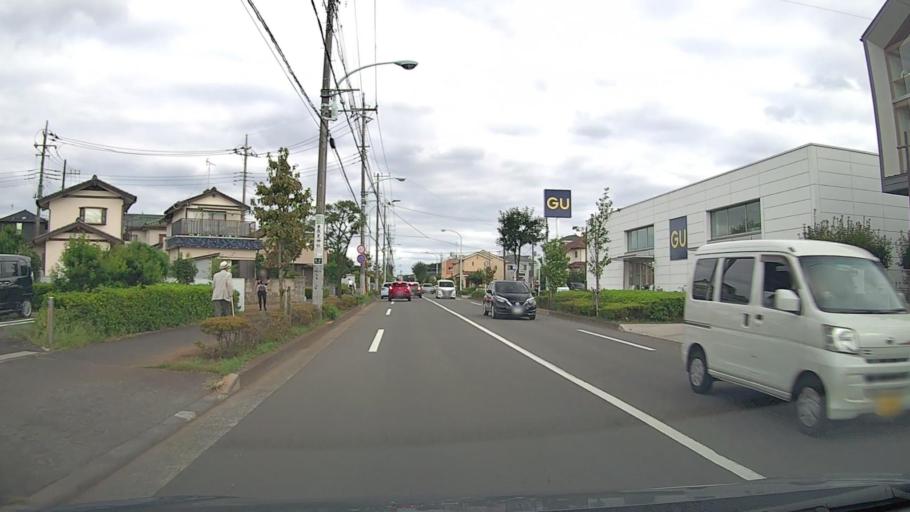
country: JP
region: Tokyo
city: Tanashicho
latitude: 35.7457
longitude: 139.5164
